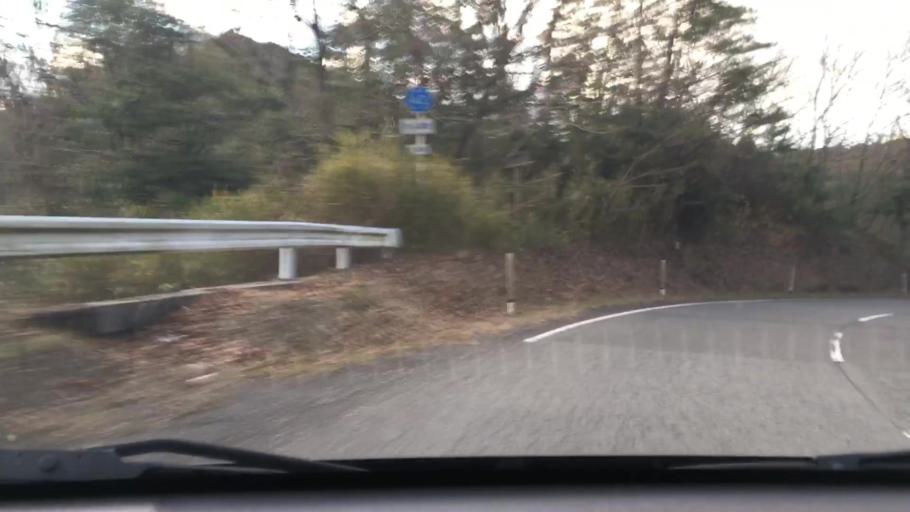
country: JP
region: Oita
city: Hiji
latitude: 33.4140
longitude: 131.4205
